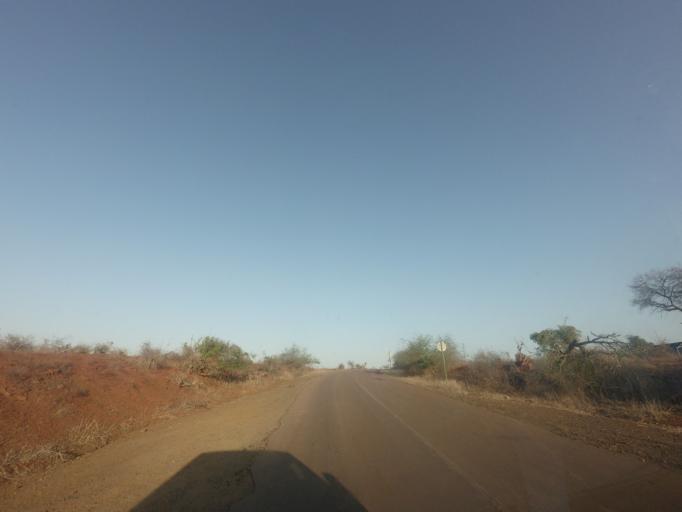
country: ZA
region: Mpumalanga
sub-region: Ehlanzeni District
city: Komatipoort
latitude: -25.3617
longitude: 31.8928
